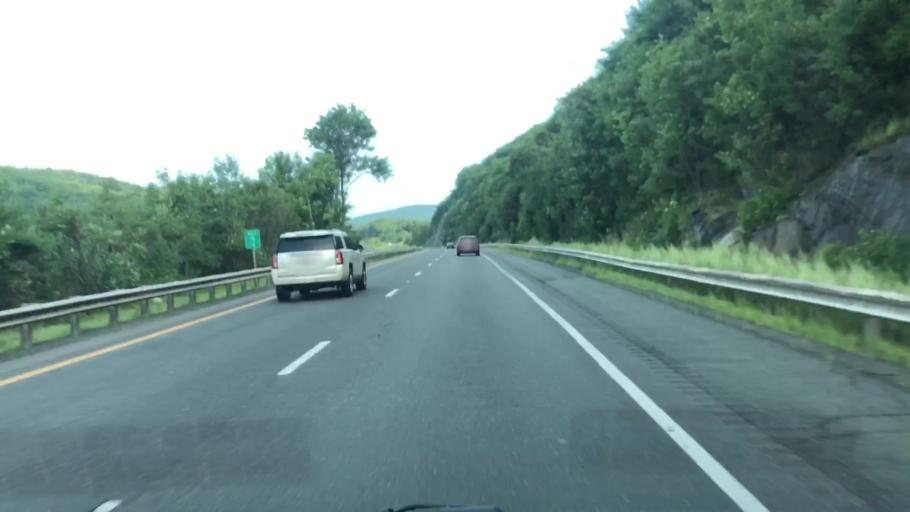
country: US
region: Massachusetts
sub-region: Berkshire County
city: Becket
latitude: 42.2721
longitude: -73.1348
